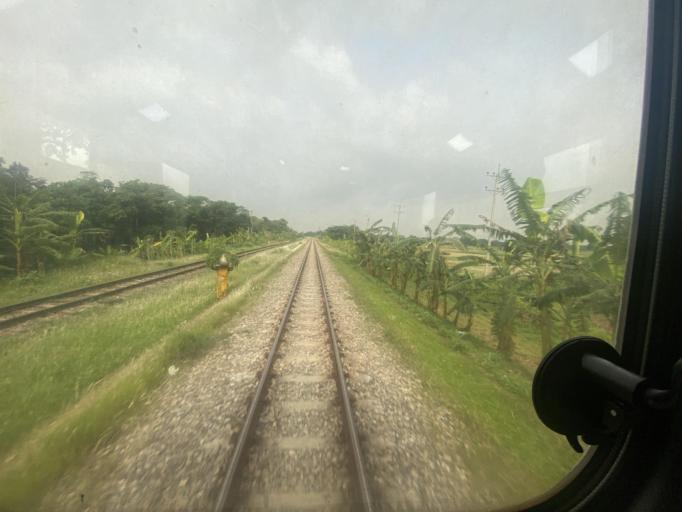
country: BD
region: Dhaka
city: Tungi
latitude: 23.9316
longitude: 90.5281
